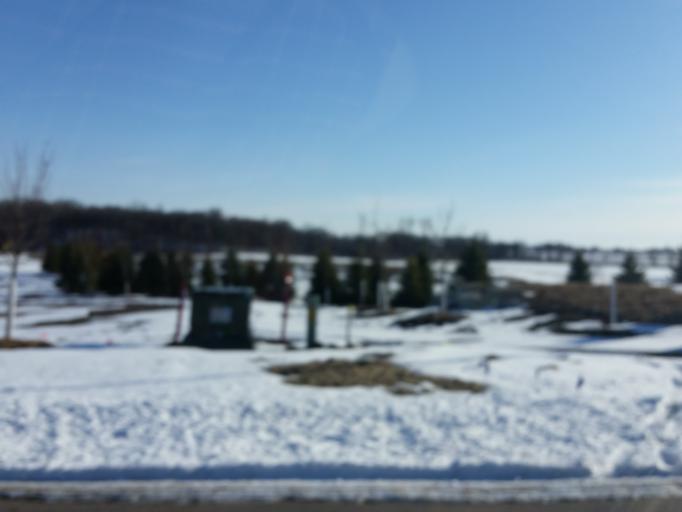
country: US
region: Minnesota
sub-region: Scott County
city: Elko New Market
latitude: 44.6293
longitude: -93.3655
